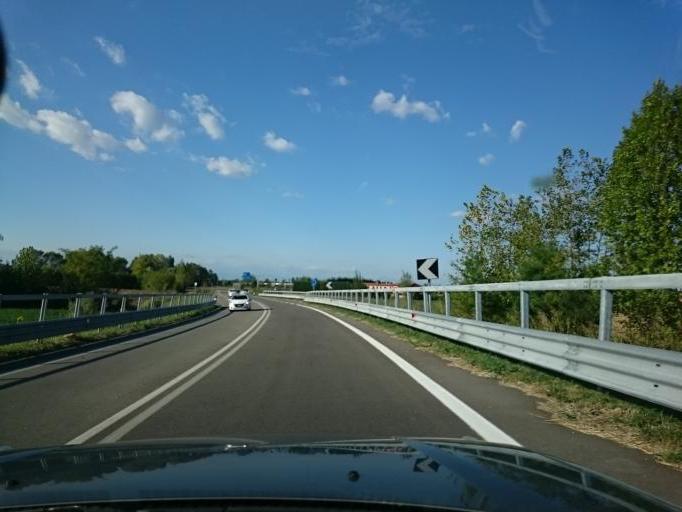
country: IT
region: Veneto
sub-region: Provincia di Padova
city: Tencarola
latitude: 45.3765
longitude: 11.8259
